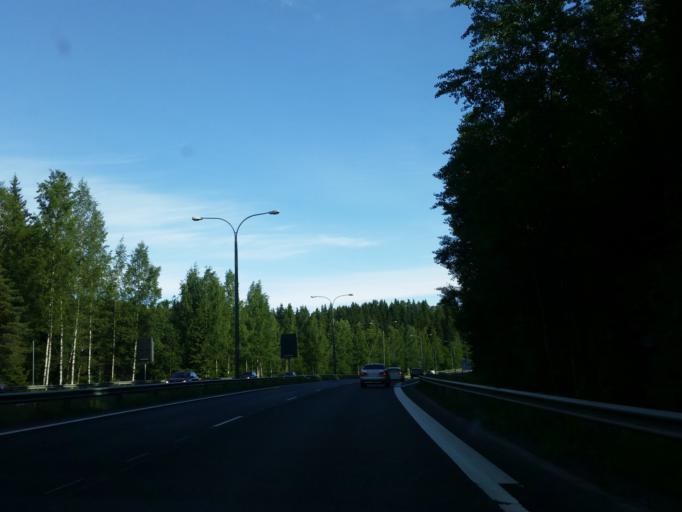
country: FI
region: Northern Savo
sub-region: Kuopio
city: Kuopio
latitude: 62.9121
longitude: 27.6852
